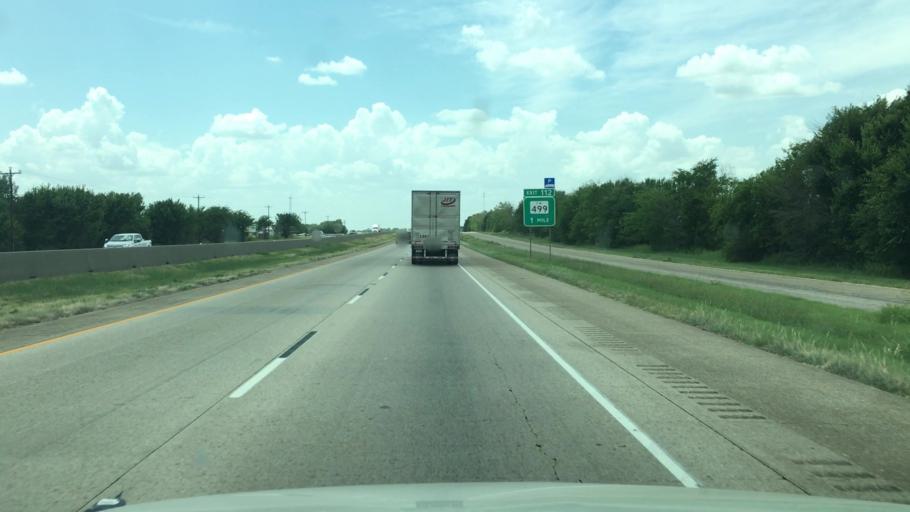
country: US
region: Texas
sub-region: Hunt County
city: Commerce
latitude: 33.1309
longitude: -95.7809
